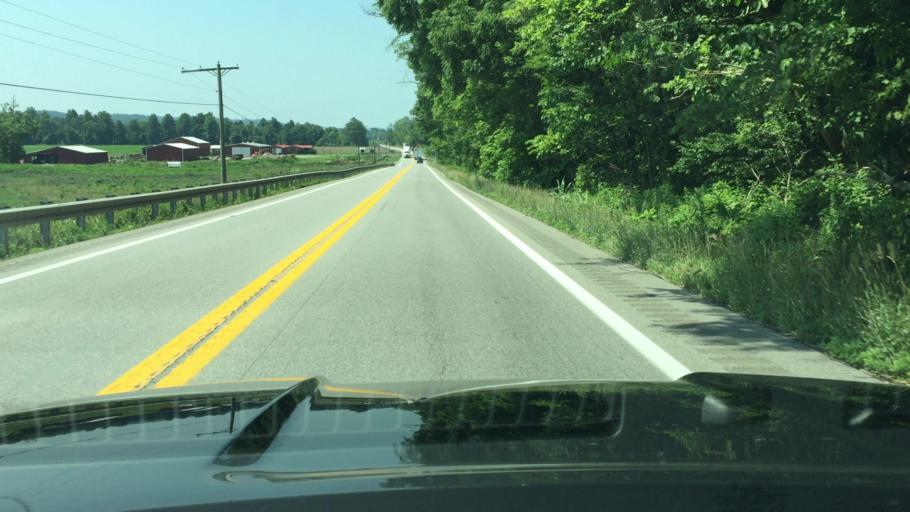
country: US
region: West Virginia
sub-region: Putnam County
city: Buffalo
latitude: 38.6433
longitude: -81.9741
